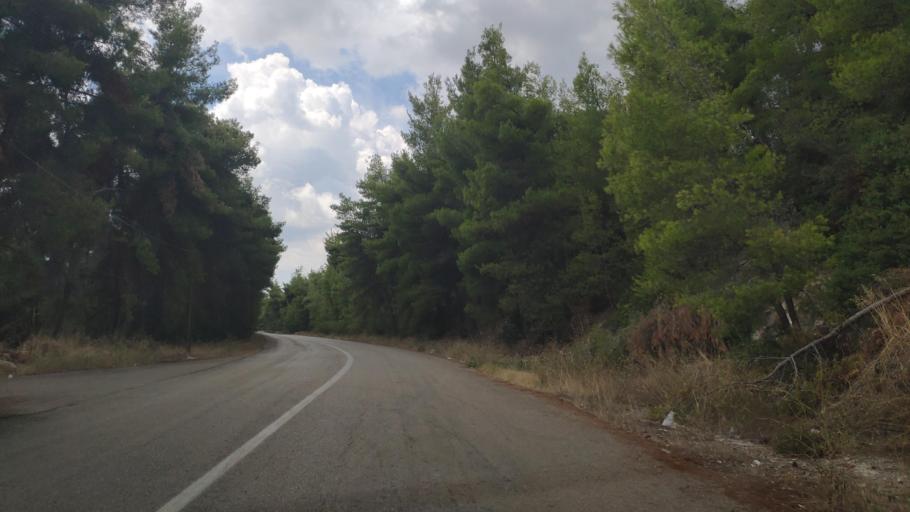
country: GR
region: Central Greece
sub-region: Nomos Fthiotidos
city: Malesina
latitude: 38.6427
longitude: 23.1990
